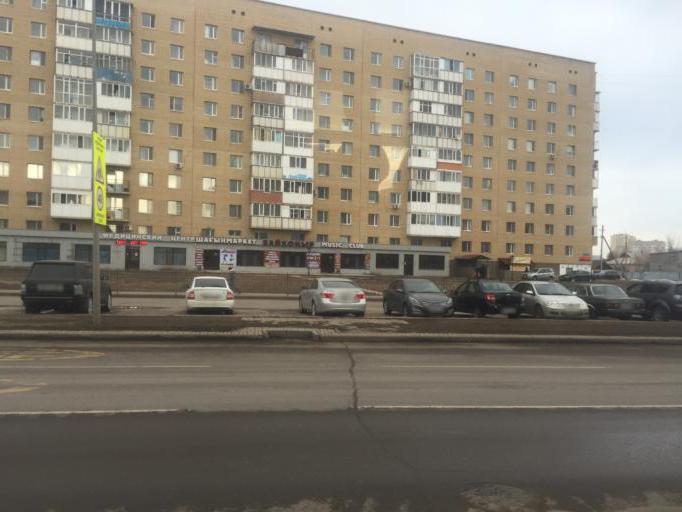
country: KZ
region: Astana Qalasy
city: Astana
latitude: 51.1702
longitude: 71.3875
